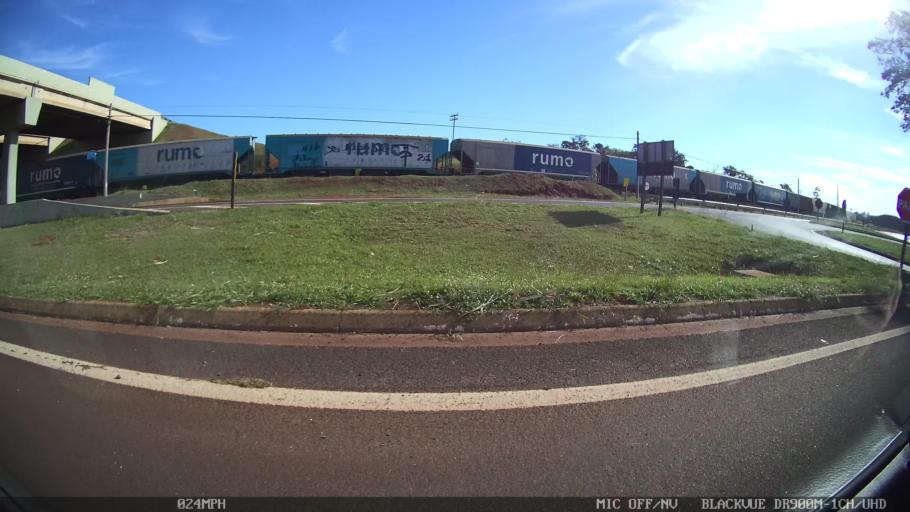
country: BR
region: Sao Paulo
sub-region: Araraquara
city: Araraquara
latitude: -21.7934
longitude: -48.1333
